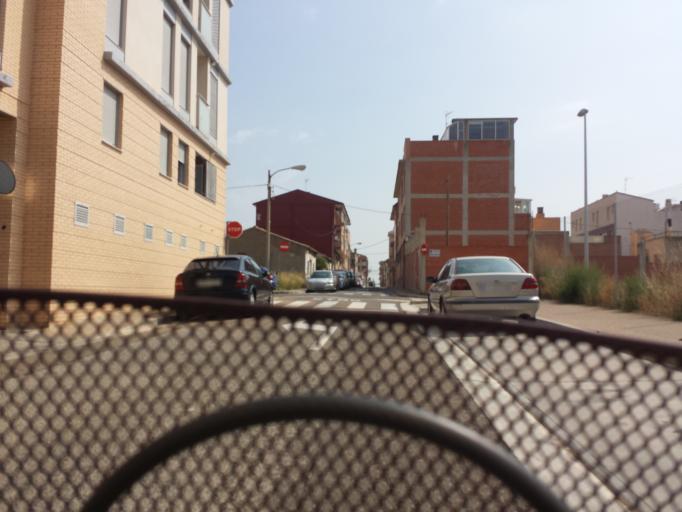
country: ES
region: Aragon
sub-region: Provincia de Zaragoza
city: Montecanal
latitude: 41.6367
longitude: -0.9350
